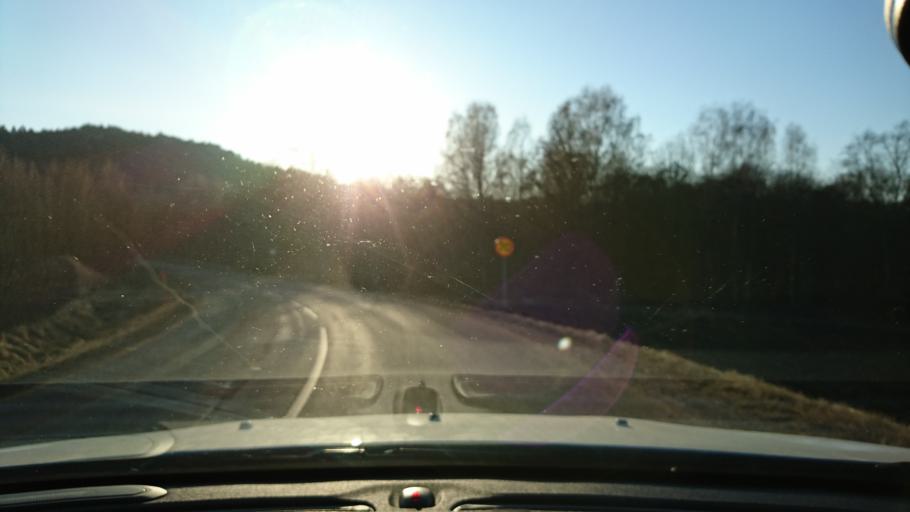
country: SE
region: Vaestra Goetaland
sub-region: Uddevalla Kommun
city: Ljungskile
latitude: 58.2011
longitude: 11.9145
